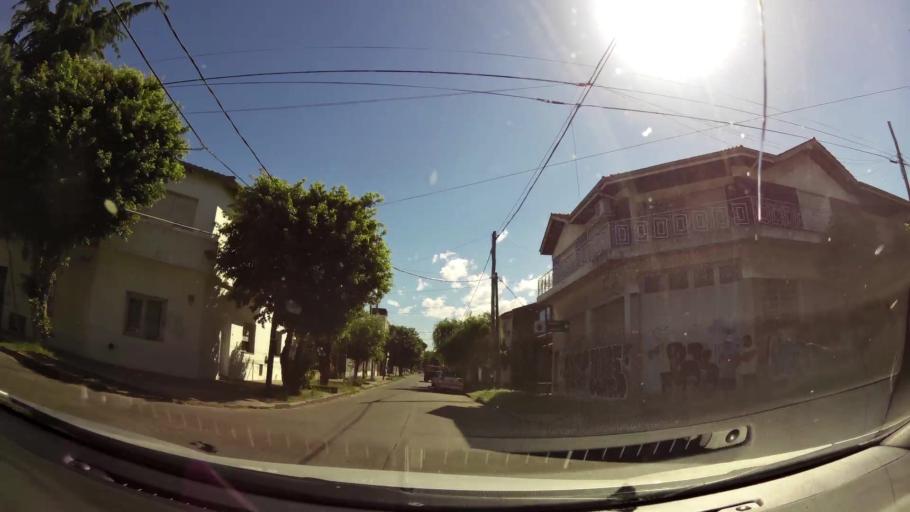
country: AR
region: Buenos Aires
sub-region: Partido de San Isidro
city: San Isidro
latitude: -34.4663
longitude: -58.5360
